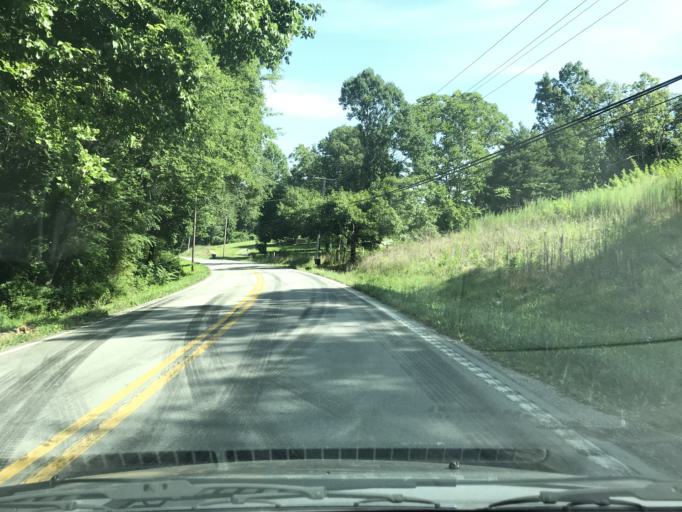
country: US
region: Tennessee
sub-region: Hamilton County
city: Lakesite
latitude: 35.2252
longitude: -85.0597
